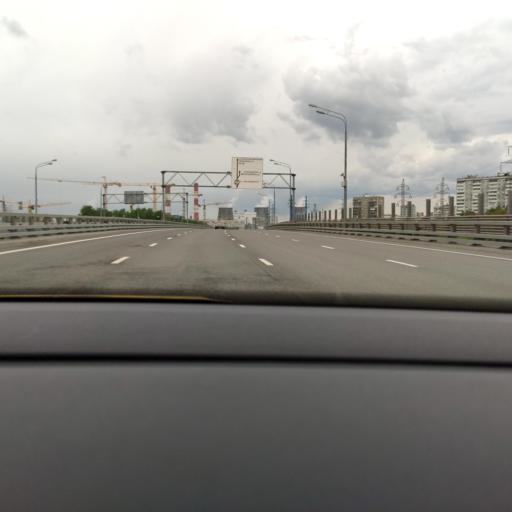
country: RU
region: Moscow
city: Amin'yevo
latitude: 55.7008
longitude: 37.4751
